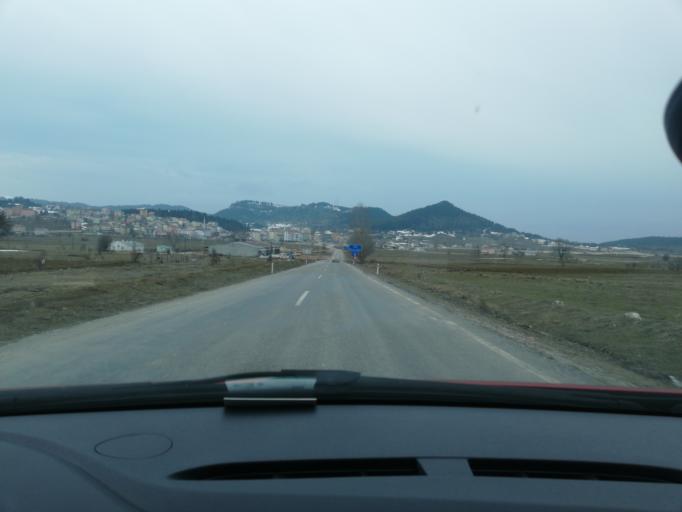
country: TR
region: Kastamonu
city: Agli
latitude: 41.6898
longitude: 33.5649
